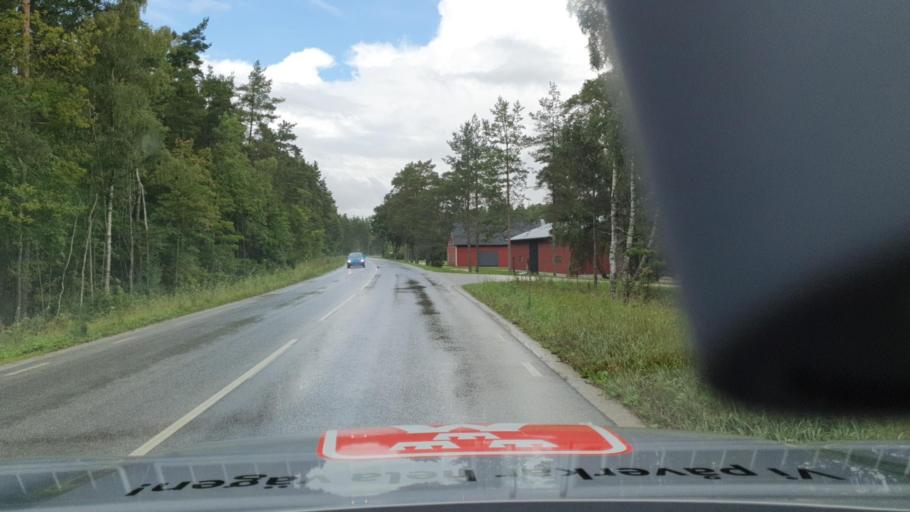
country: SE
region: Gotland
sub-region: Gotland
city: Visby
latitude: 57.5787
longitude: 18.5005
